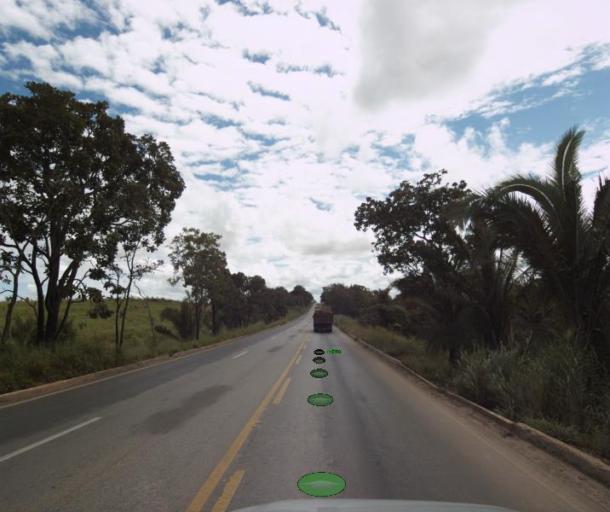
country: BR
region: Goias
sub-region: Uruacu
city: Uruacu
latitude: -14.3790
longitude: -49.1580
